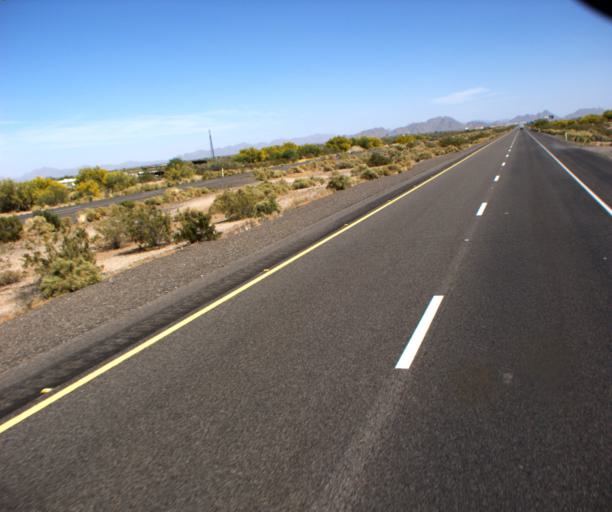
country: US
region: Arizona
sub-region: Maricopa County
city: Gila Bend
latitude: 32.9312
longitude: -112.6989
